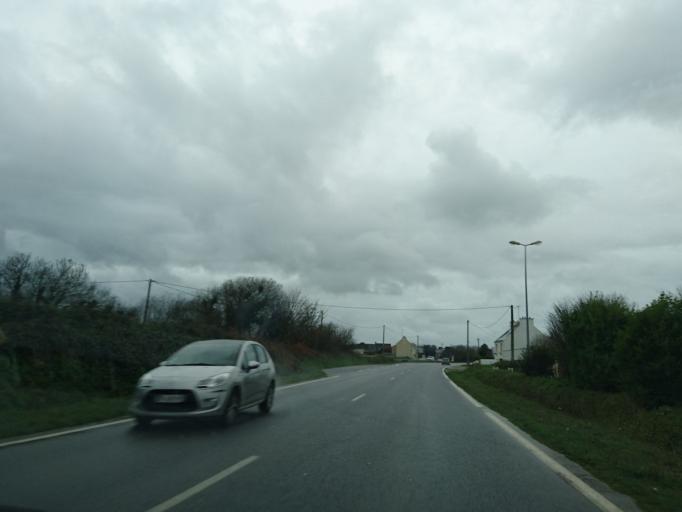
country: FR
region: Brittany
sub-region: Departement du Finistere
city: Plouzane
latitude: 48.3588
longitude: -4.6371
